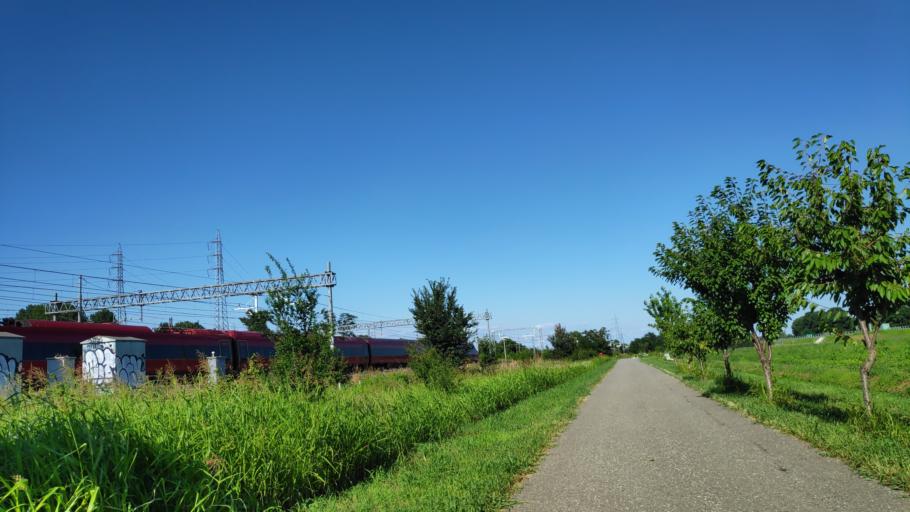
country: IT
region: Lombardy
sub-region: Citta metropolitana di Milano
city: Pozzuolo Martesana
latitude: 45.5066
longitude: 9.4474
